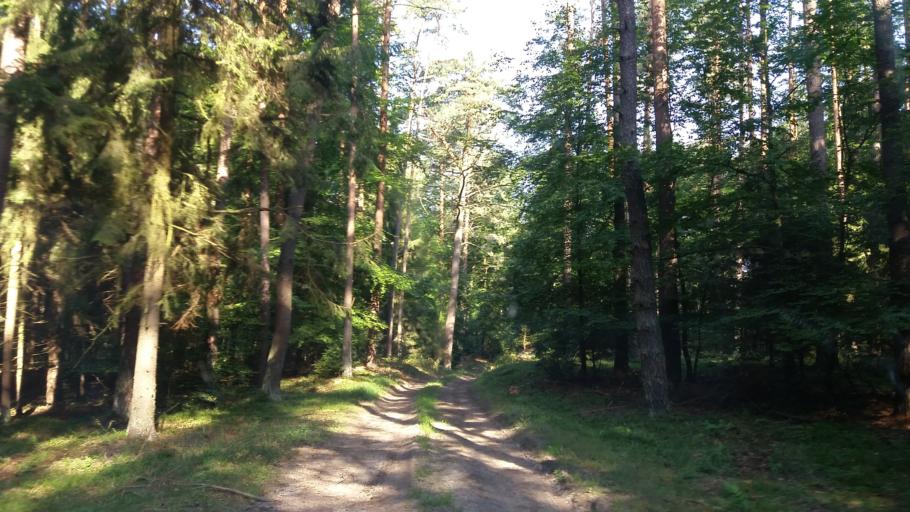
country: PL
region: West Pomeranian Voivodeship
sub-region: Powiat choszczenski
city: Pelczyce
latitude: 52.9679
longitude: 15.3589
